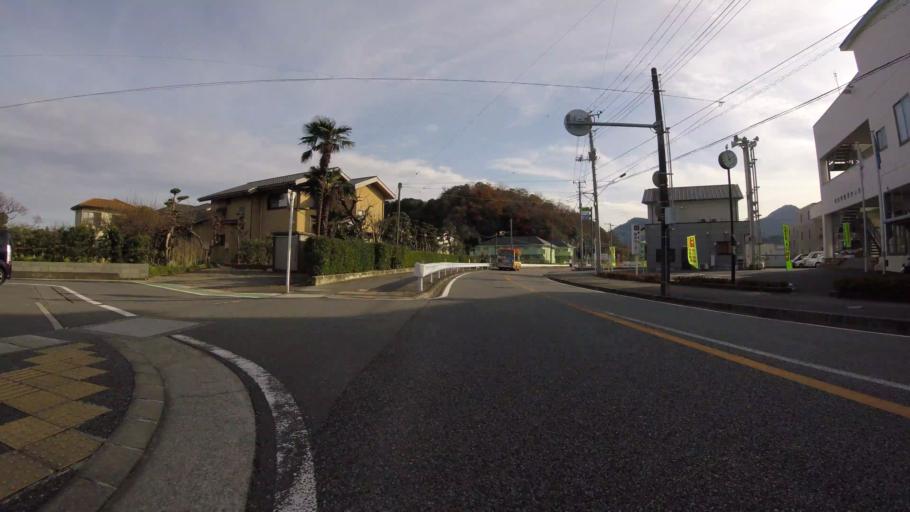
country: JP
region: Shizuoka
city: Mishima
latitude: 35.0886
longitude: 138.8987
